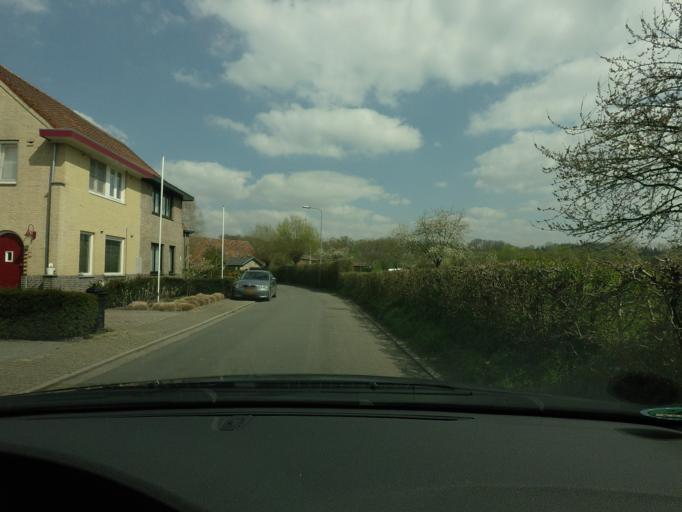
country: NL
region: Limburg
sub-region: Eijsden-Margraten
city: Eijsden
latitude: 50.7627
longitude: 5.7364
